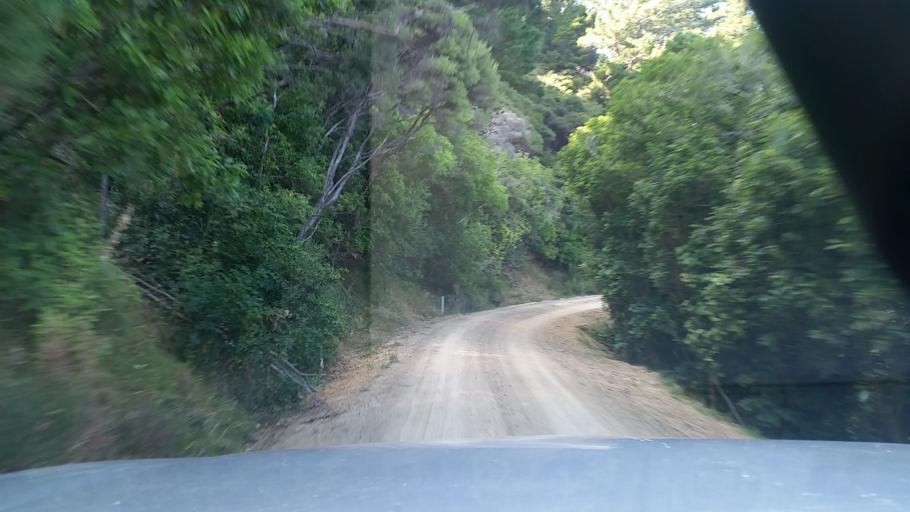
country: NZ
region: Marlborough
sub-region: Marlborough District
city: Picton
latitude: -41.3106
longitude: 174.1714
